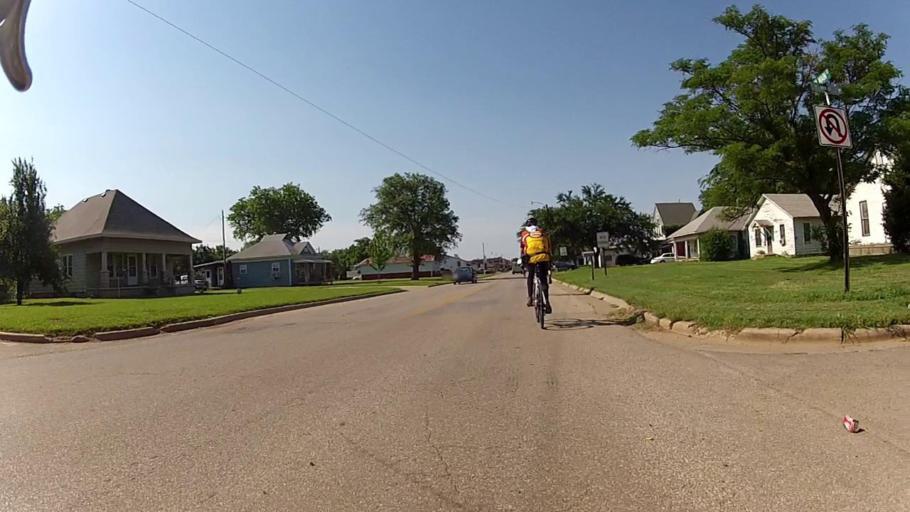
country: US
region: Kansas
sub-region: Sumner County
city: Caldwell
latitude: 37.0358
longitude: -97.6070
